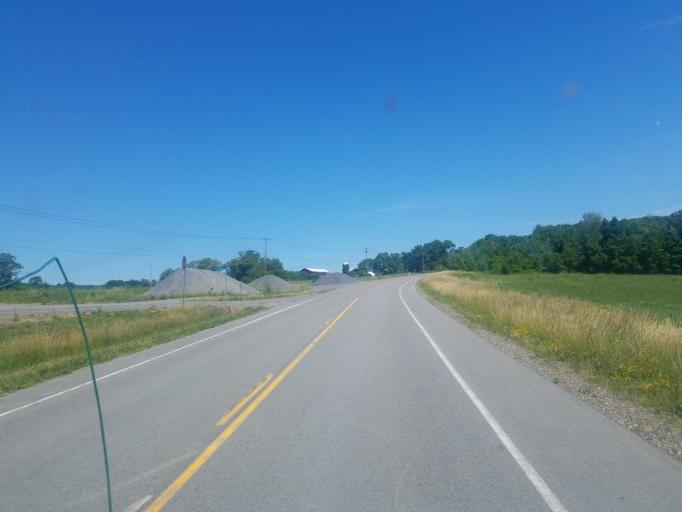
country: US
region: New York
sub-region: Ontario County
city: Canandaigua
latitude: 42.7241
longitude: -77.2790
